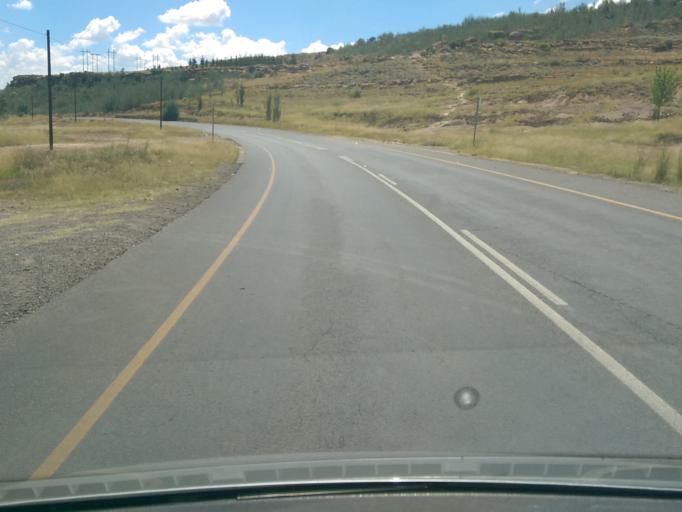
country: LS
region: Maseru
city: Maseru
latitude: -29.3805
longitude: 27.5026
